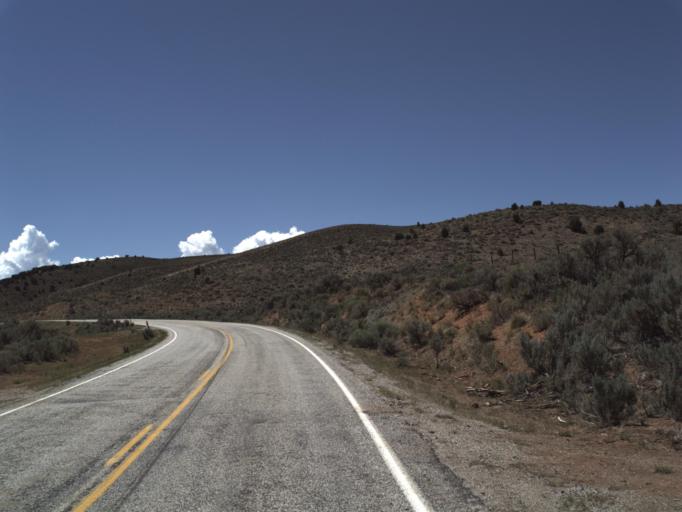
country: US
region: Utah
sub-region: Rich County
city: Randolph
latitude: 41.5023
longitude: -111.2837
